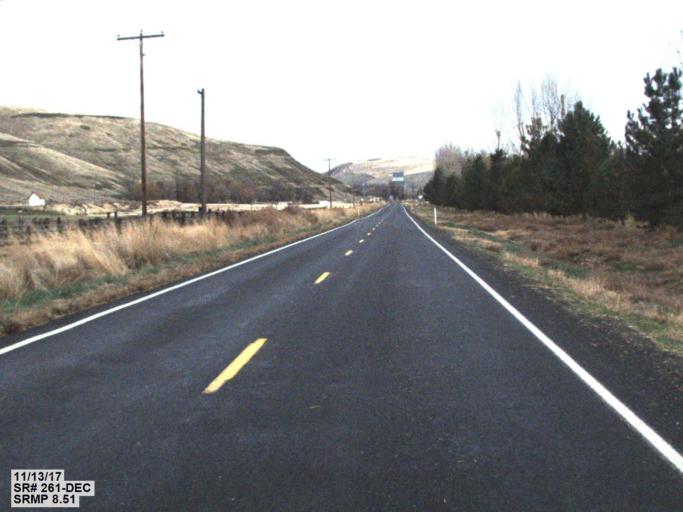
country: US
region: Washington
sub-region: Walla Walla County
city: Waitsburg
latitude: 46.5250
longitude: -118.1348
